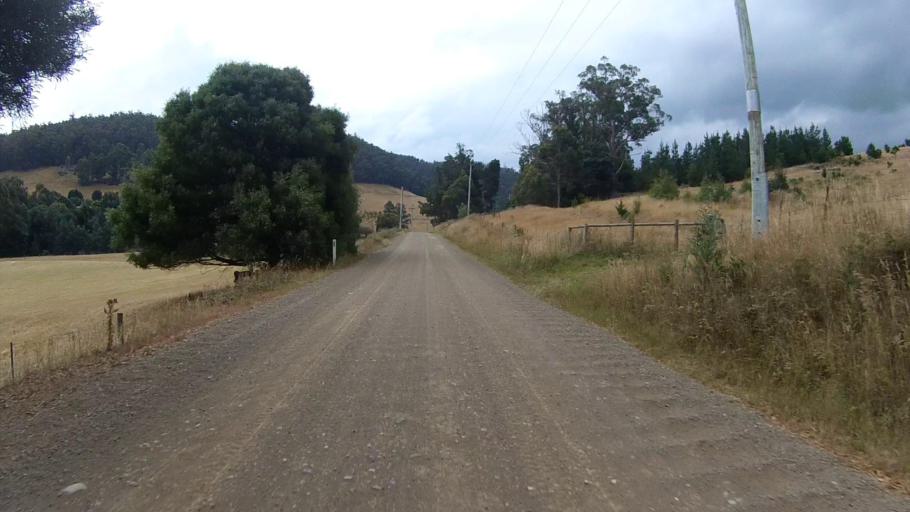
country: AU
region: Tasmania
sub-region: Huon Valley
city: Huonville
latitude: -42.9730
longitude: 147.0542
